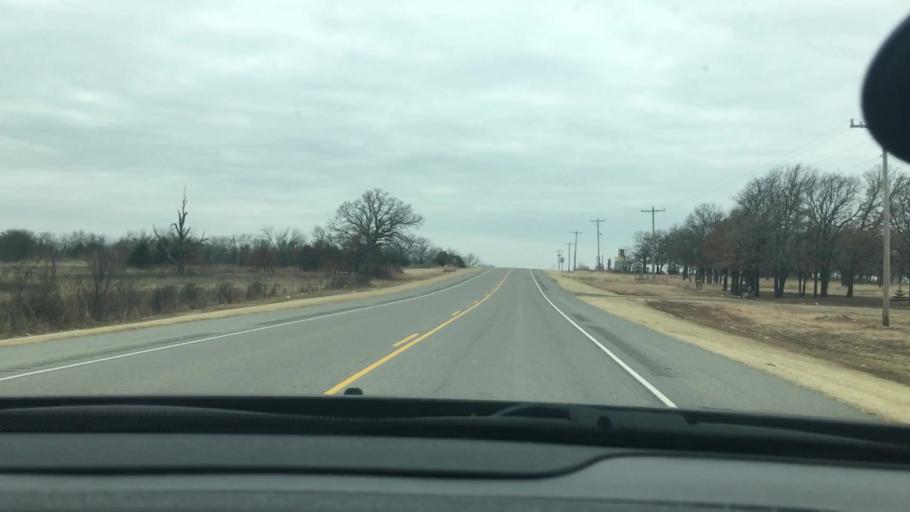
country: US
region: Oklahoma
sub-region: Carter County
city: Healdton
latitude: 34.4880
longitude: -97.4513
